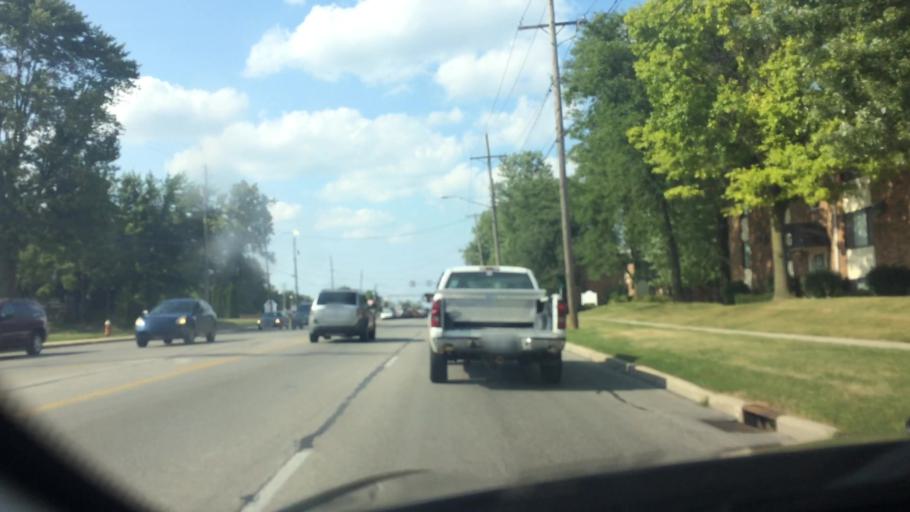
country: US
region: Ohio
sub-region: Lucas County
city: Ottawa Hills
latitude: 41.6218
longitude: -83.6257
